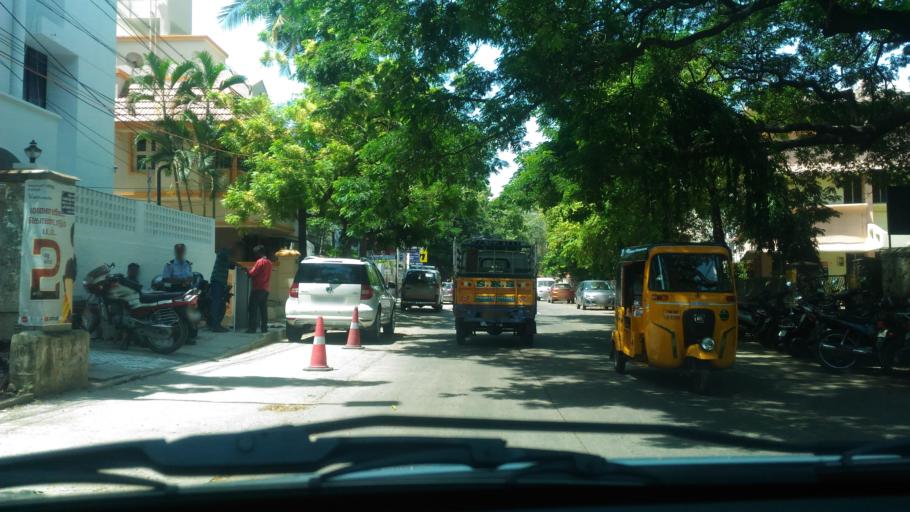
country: IN
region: Tamil Nadu
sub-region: Chennai
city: Chetput
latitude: 13.0499
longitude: 80.2456
